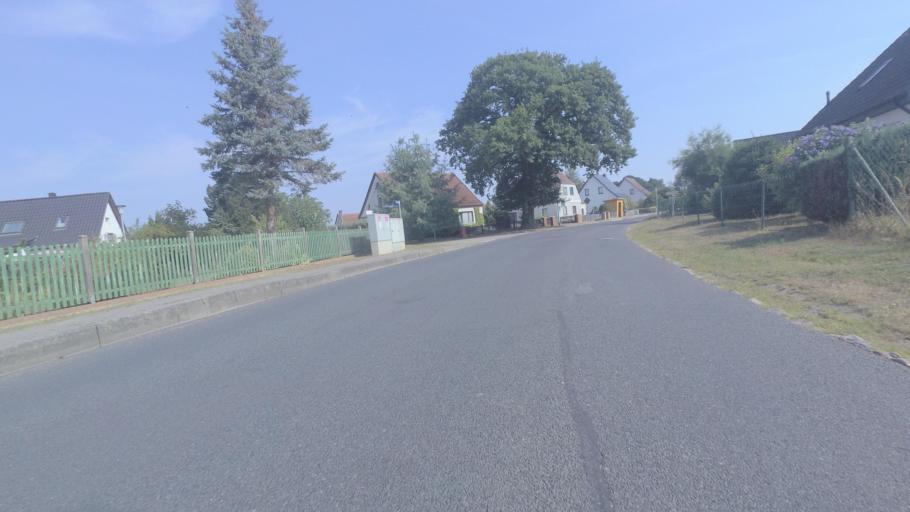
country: DE
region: Mecklenburg-Vorpommern
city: Wendorf
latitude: 54.2354
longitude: 13.0665
